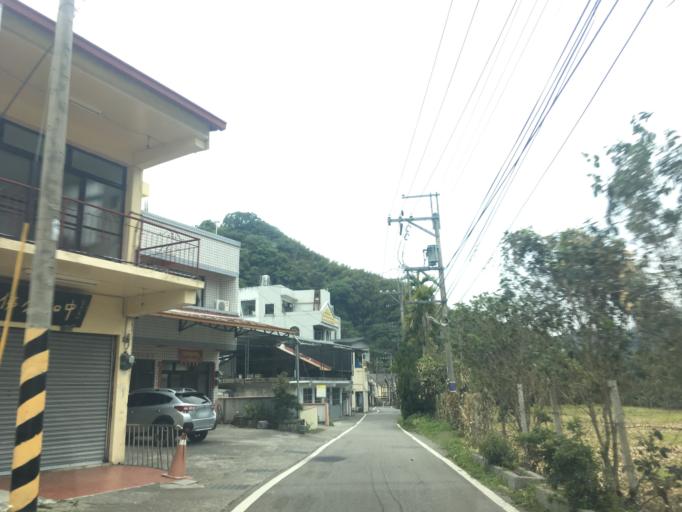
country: TW
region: Taiwan
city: Fengyuan
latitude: 24.1579
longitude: 120.8274
